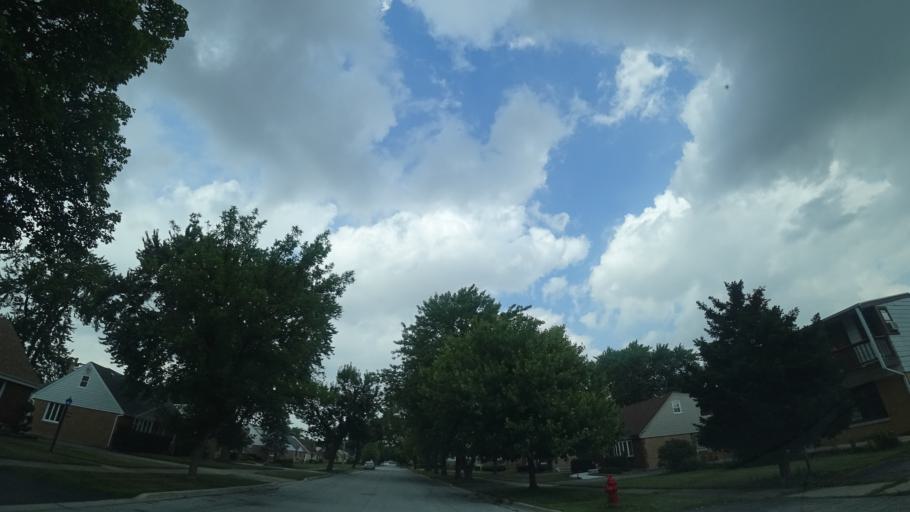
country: US
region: Illinois
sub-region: Cook County
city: Chicago Ridge
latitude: 41.6948
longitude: -87.7704
